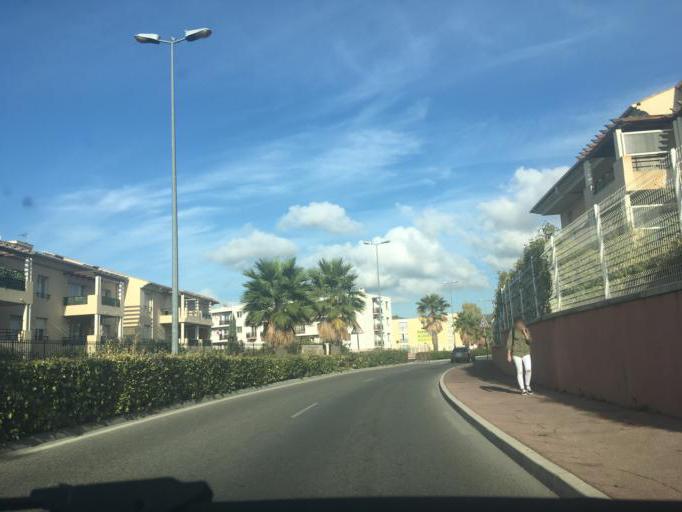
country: FR
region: Provence-Alpes-Cote d'Azur
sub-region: Departement du Var
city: Draguignan
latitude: 43.5301
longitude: 6.4667
